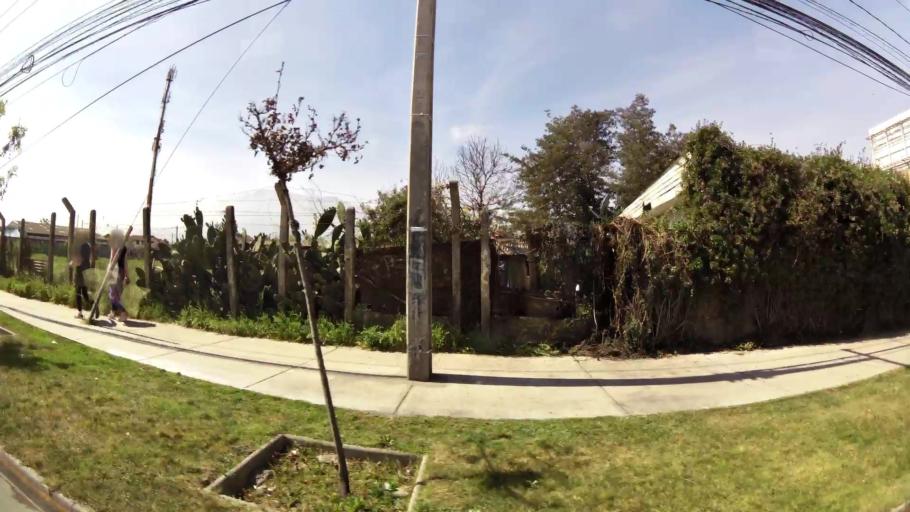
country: CL
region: Santiago Metropolitan
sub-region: Provincia de Cordillera
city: Puente Alto
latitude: -33.5960
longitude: -70.5783
